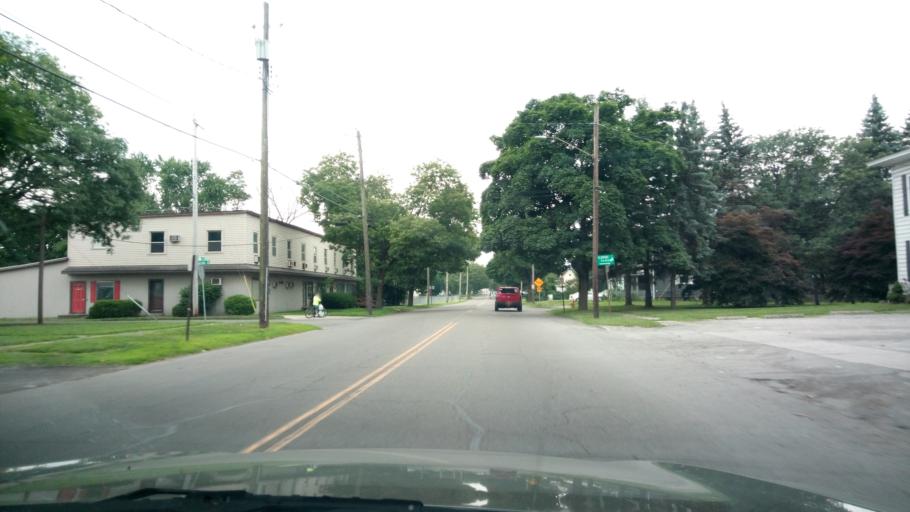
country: US
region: New York
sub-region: Chemung County
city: Elmira Heights
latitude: 42.1137
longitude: -76.8078
